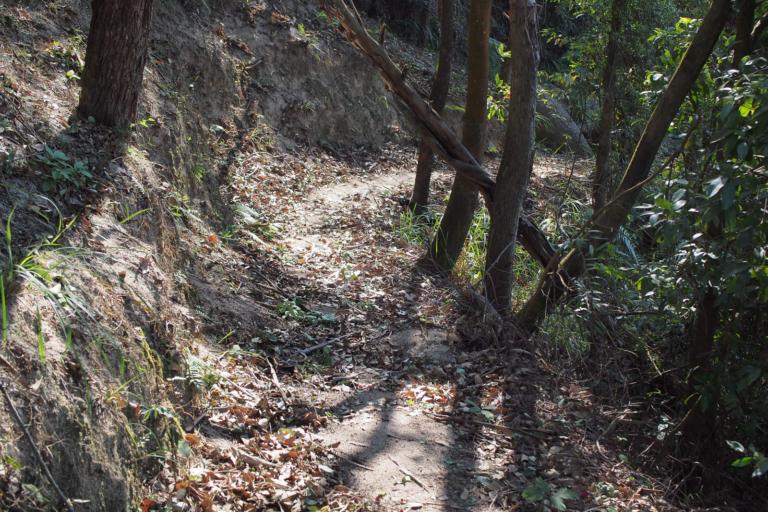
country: CN
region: Guangdong
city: Huancheng
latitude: 22.4614
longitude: 113.4141
